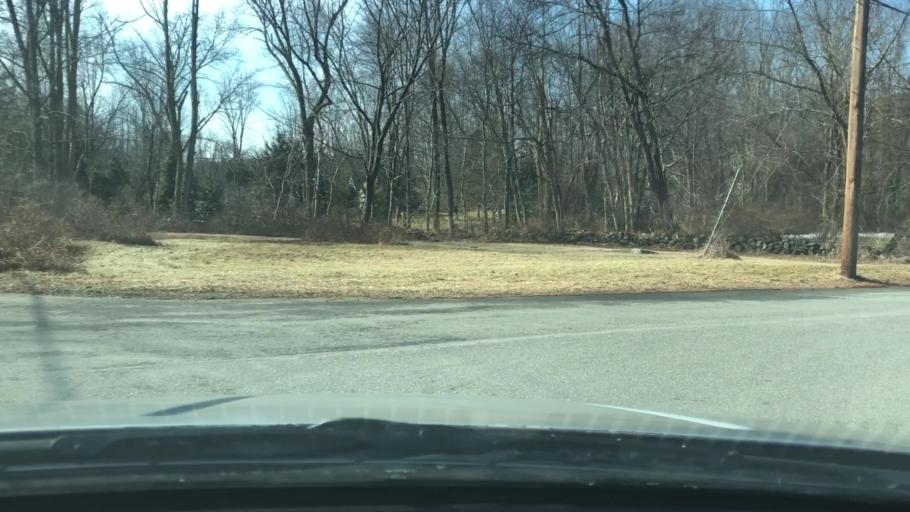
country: US
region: Massachusetts
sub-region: Middlesex County
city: West Concord
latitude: 42.4982
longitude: -71.3894
